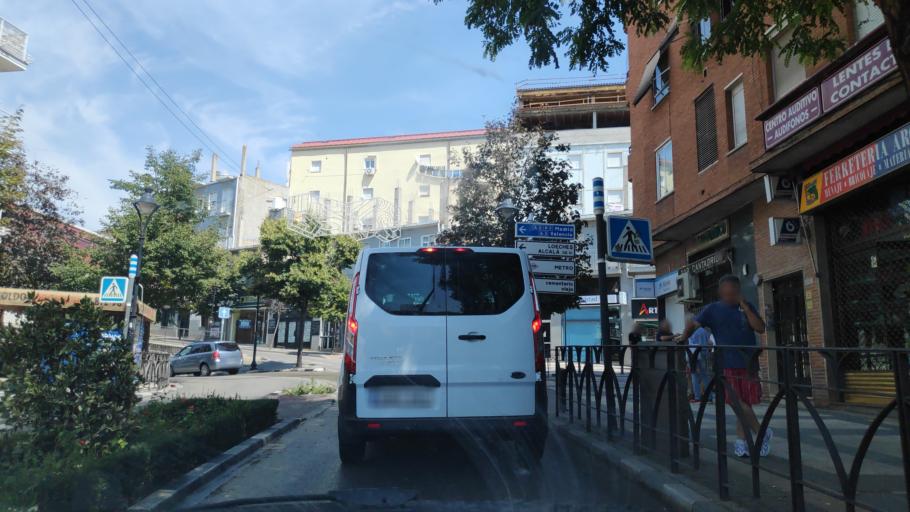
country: ES
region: Madrid
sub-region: Provincia de Madrid
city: Arganda
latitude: 40.3017
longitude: -3.4412
